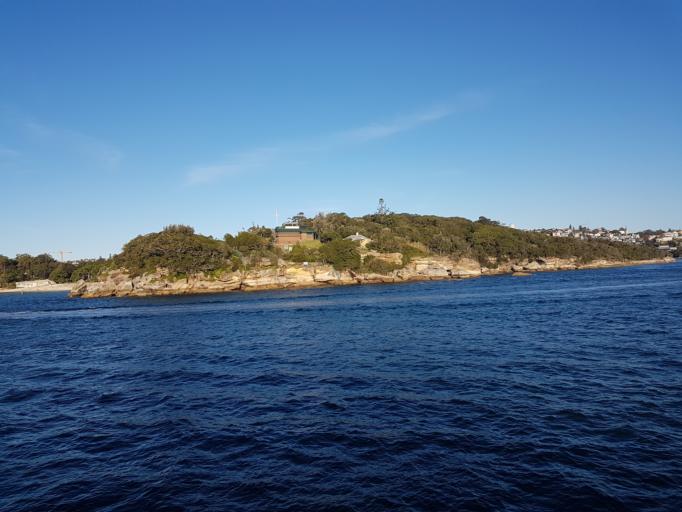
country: AU
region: New South Wales
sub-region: Woollahra
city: Point Piper
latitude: -33.8504
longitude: 151.2625
